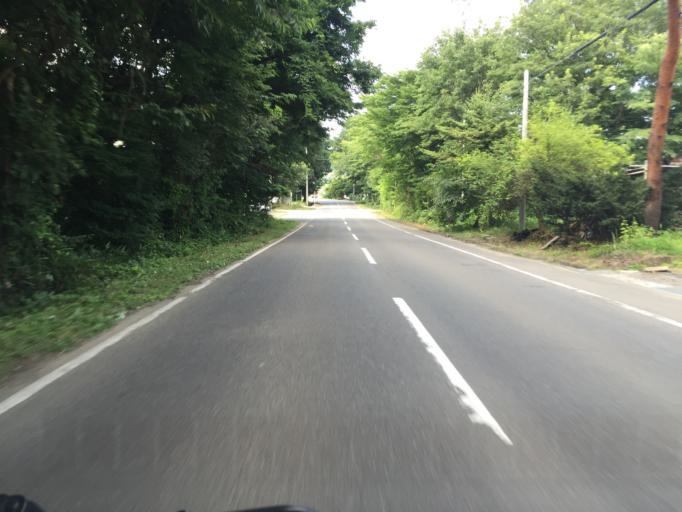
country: JP
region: Fukushima
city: Fukushima-shi
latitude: 37.7642
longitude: 140.3613
